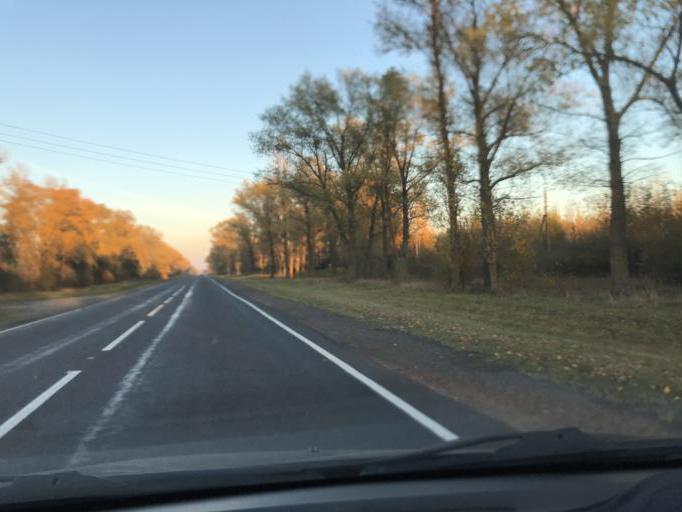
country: BY
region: Minsk
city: Staryya Darohi
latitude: 53.0584
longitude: 28.4607
